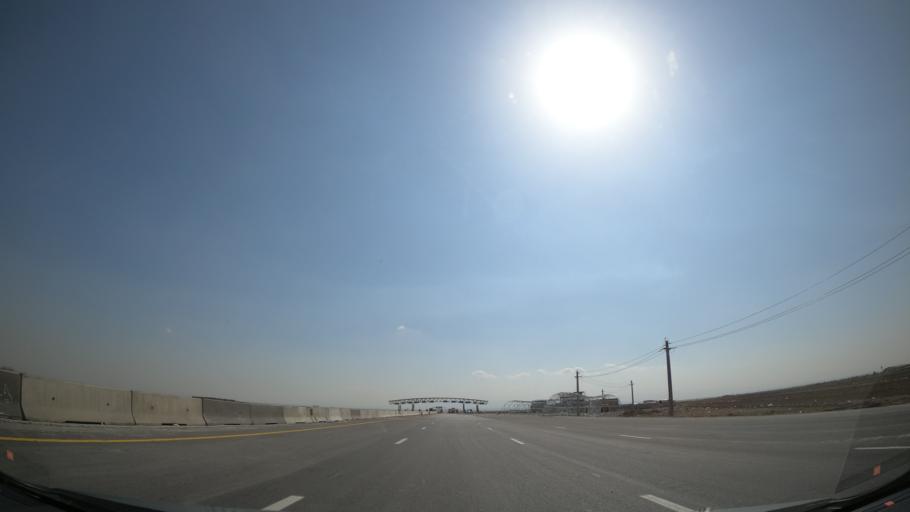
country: IR
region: Qazvin
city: Abyek
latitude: 35.9610
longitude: 50.4637
